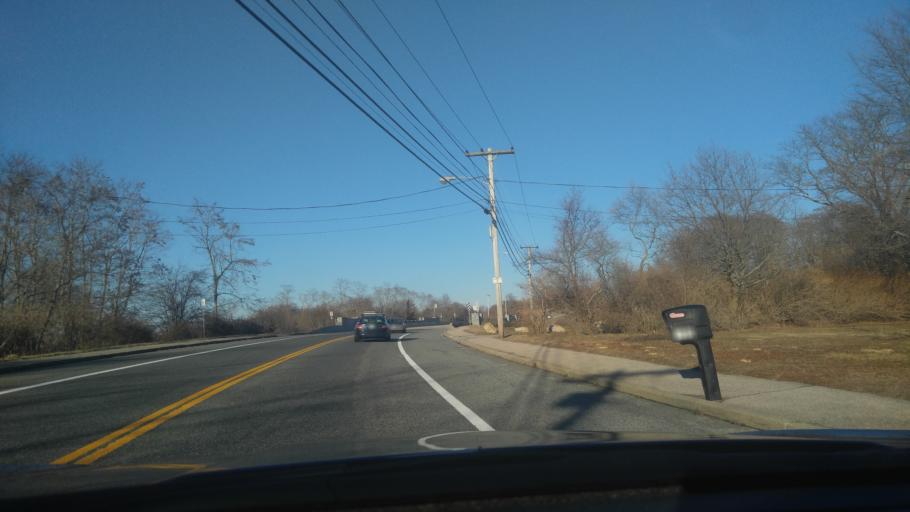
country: US
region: Rhode Island
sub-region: Washington County
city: Narragansett Pier
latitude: 41.4482
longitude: -71.4508
